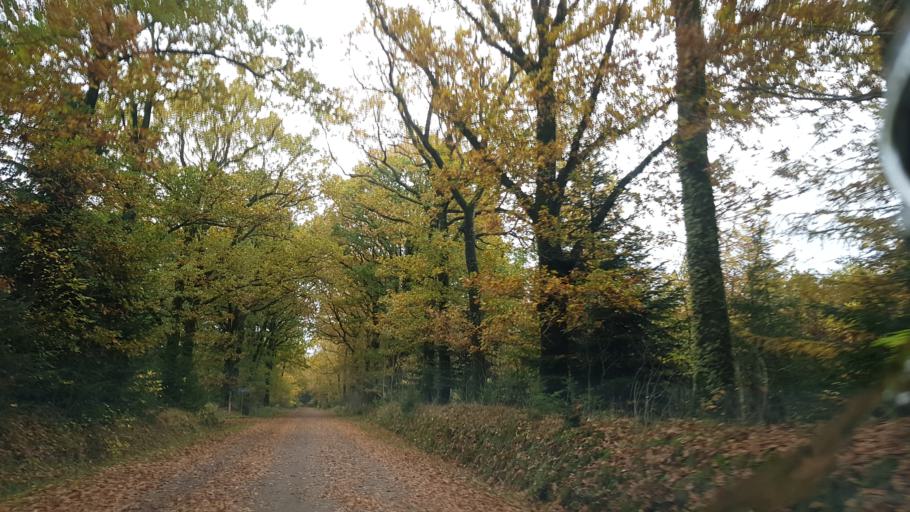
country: DK
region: South Denmark
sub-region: Tonder Kommune
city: Sherrebek
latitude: 55.1803
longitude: 8.7655
